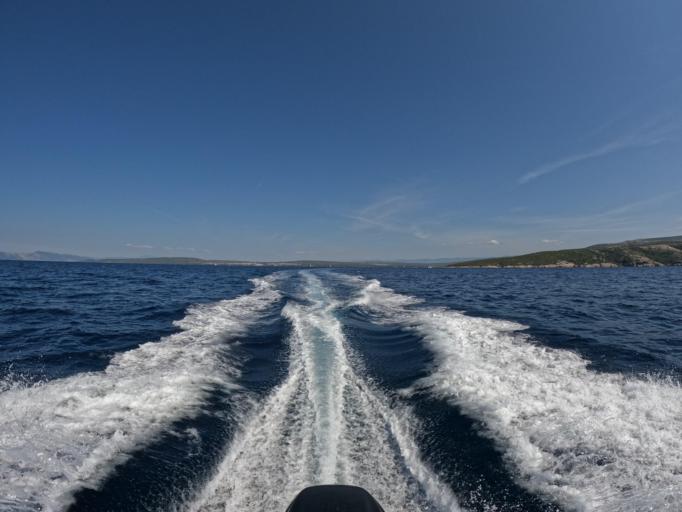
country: HR
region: Primorsko-Goranska
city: Punat
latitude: 44.9651
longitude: 14.6067
